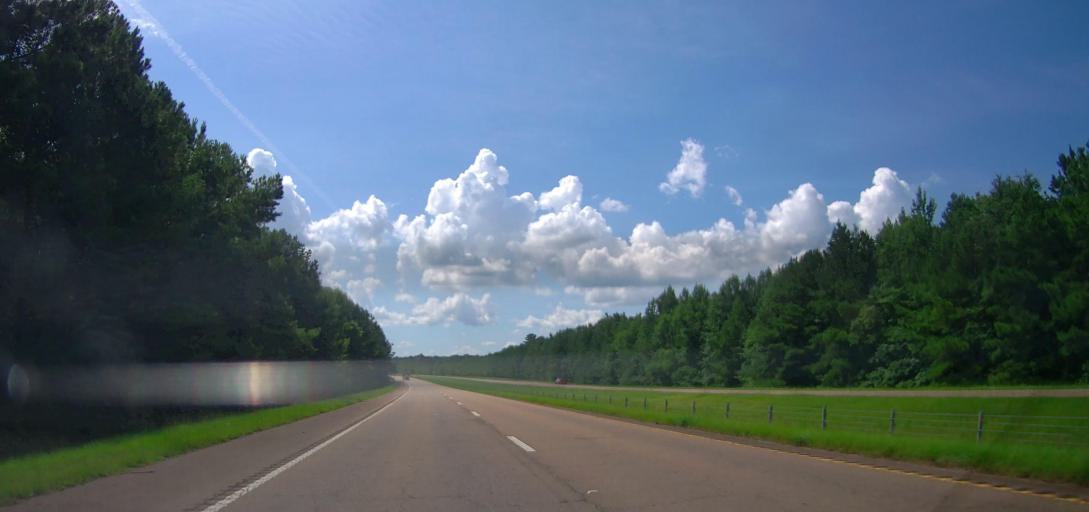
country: US
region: Mississippi
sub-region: Lowndes County
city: New Hope
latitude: 33.5048
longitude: -88.3132
